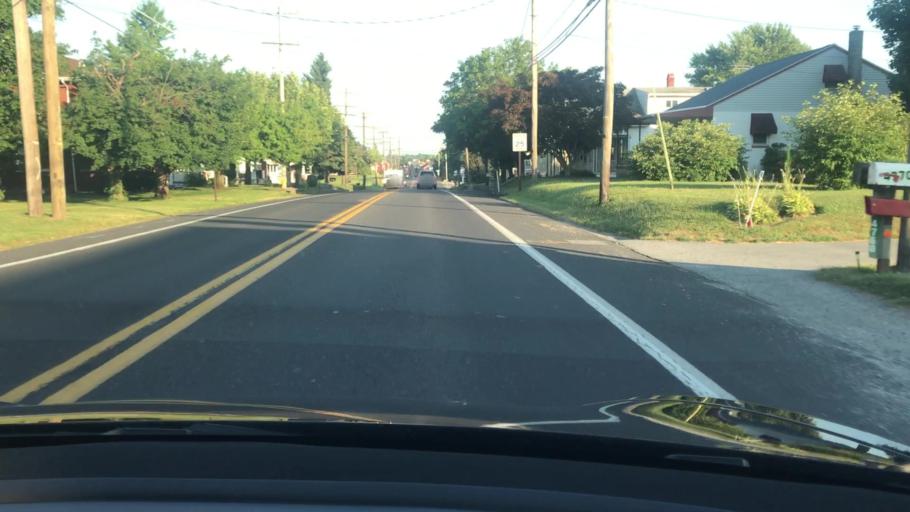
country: US
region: Pennsylvania
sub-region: York County
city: Dover
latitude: 40.0069
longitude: -76.8562
